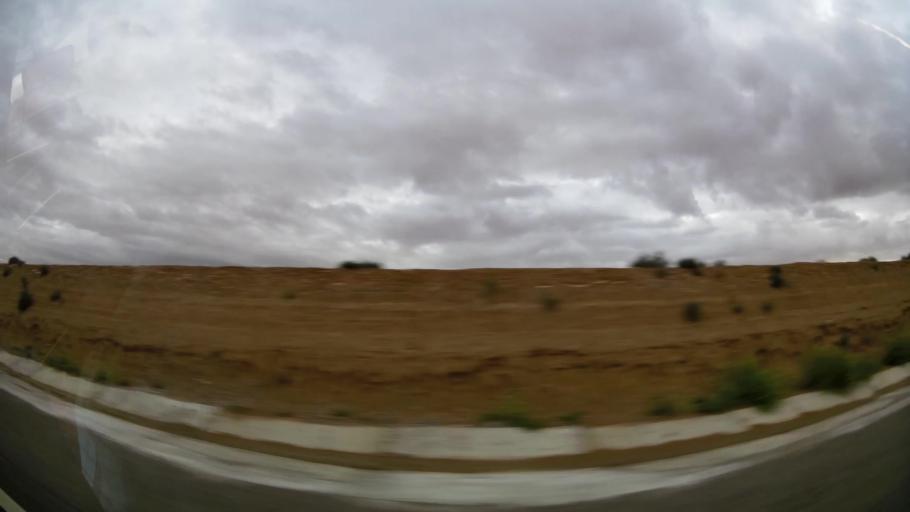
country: MA
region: Taza-Al Hoceima-Taounate
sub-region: Taza
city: Guercif
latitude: 34.3048
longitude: -3.6554
